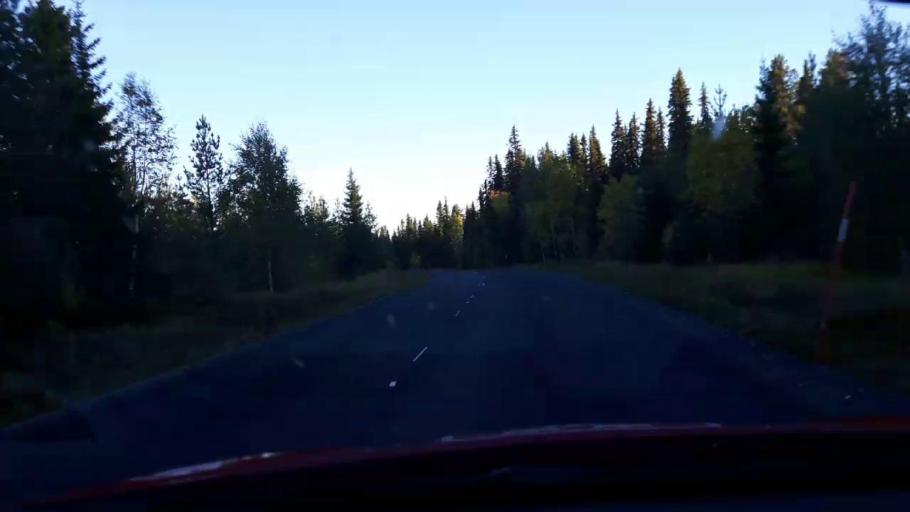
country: SE
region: Jaemtland
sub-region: OEstersunds Kommun
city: Lit
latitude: 63.4070
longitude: 14.8793
